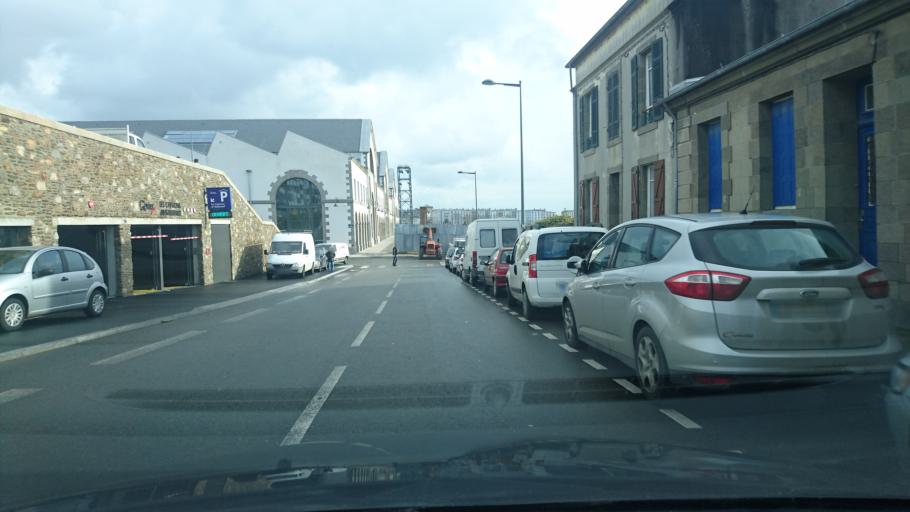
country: FR
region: Brittany
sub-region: Departement du Finistere
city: Brest
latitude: 48.3894
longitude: -4.5003
